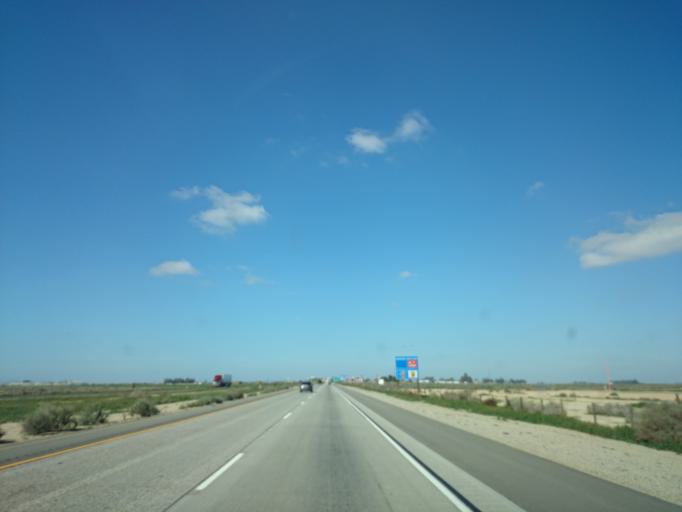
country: US
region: California
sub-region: Kern County
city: Buttonwillow
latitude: 35.3900
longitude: -119.3848
